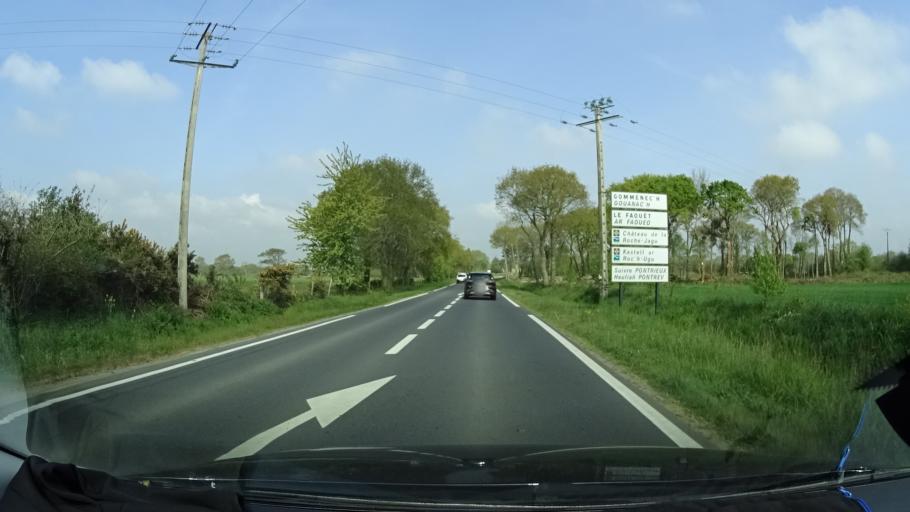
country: FR
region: Brittany
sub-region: Departement des Cotes-d'Armor
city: Lanvollon
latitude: 48.6467
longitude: -3.0067
